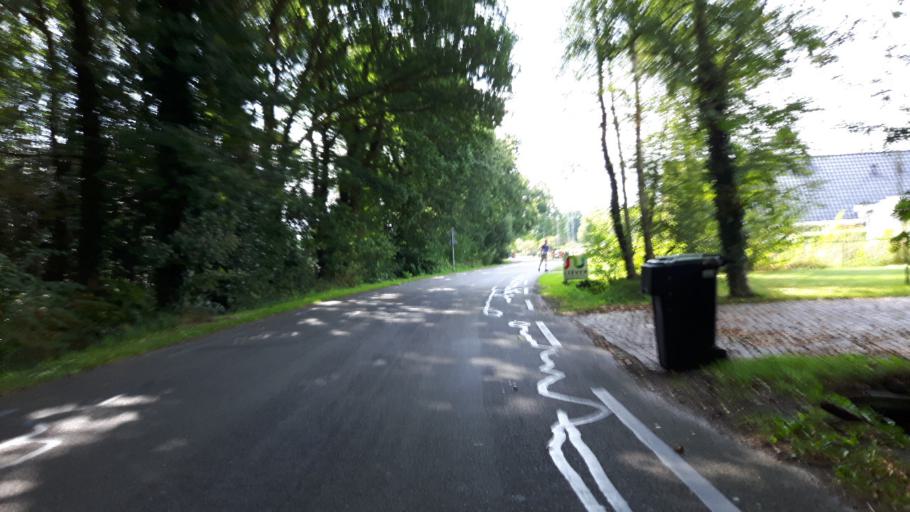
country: NL
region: Groningen
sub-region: Gemeente Leek
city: Leek
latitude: 53.1183
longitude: 6.4492
